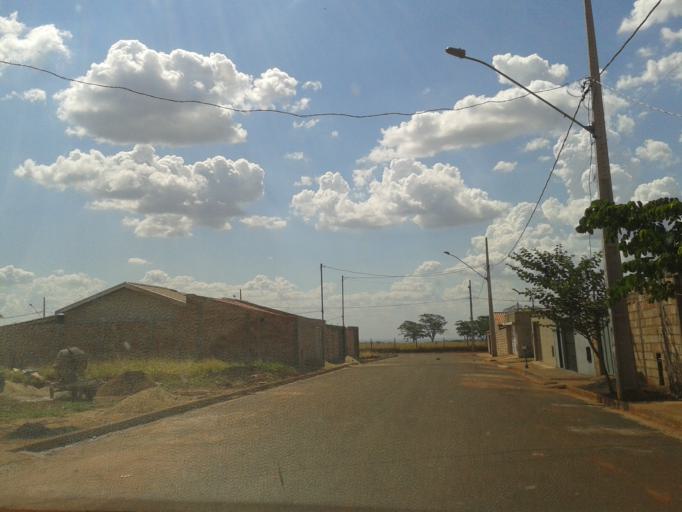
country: BR
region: Minas Gerais
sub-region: Centralina
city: Centralina
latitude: -18.7157
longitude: -49.2074
